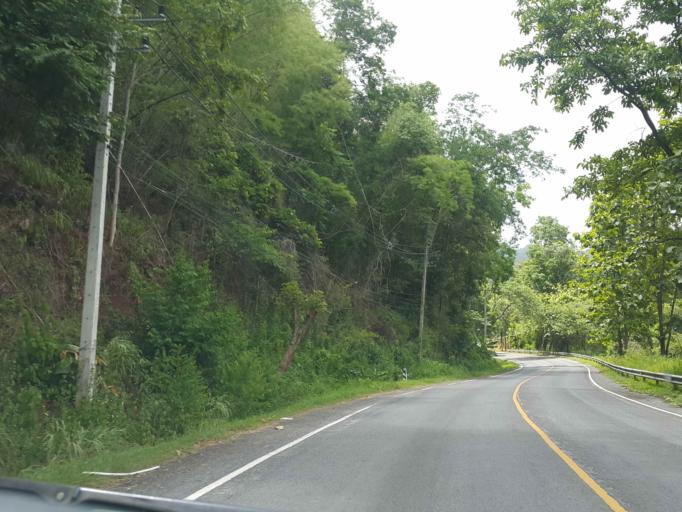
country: TH
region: Chiang Mai
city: Samoeng
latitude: 18.8123
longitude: 98.7894
